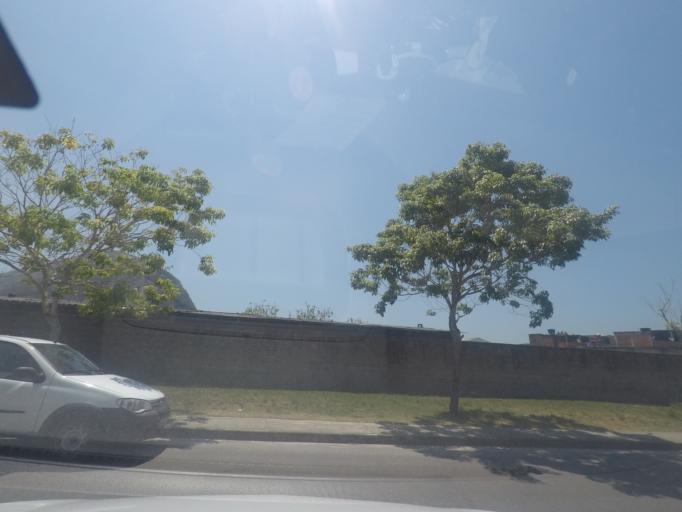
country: BR
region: Rio de Janeiro
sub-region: Nilopolis
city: Nilopolis
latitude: -22.9882
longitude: -43.4613
